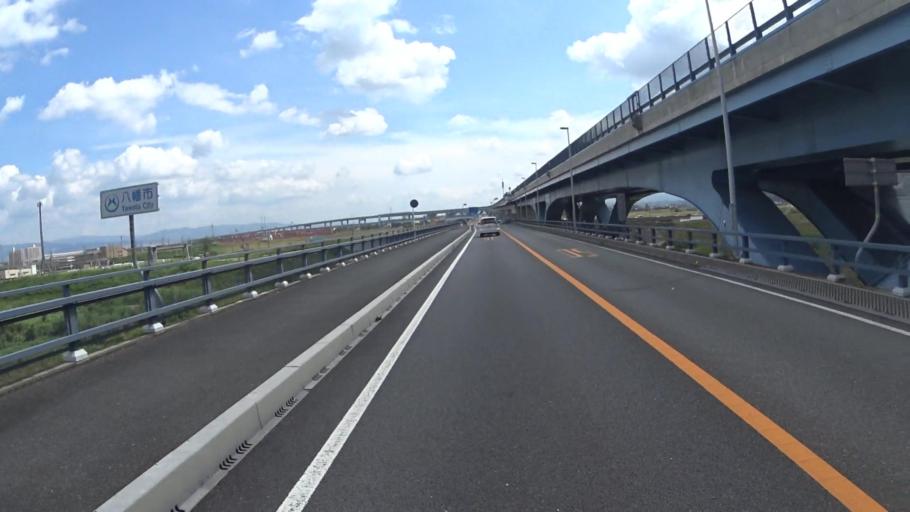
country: JP
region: Kyoto
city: Yawata
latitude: 34.8976
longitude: 135.7012
